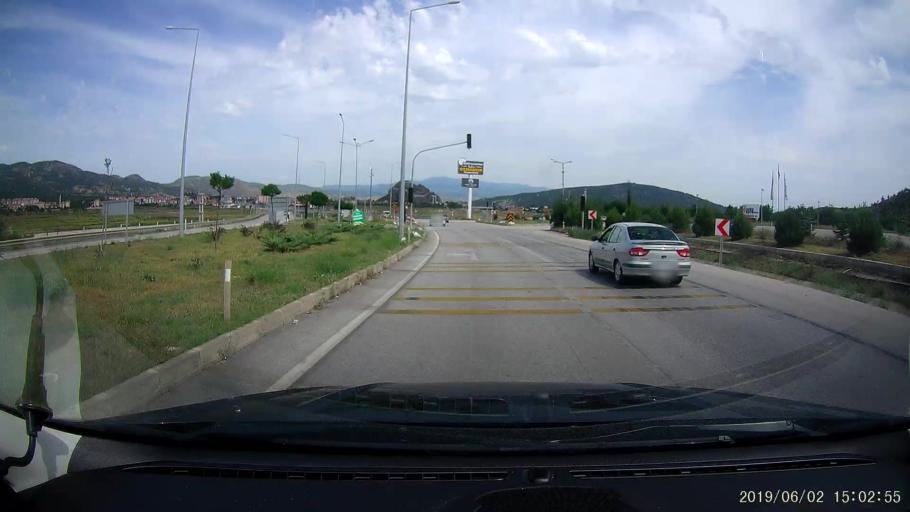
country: TR
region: Corum
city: Osmancik
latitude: 40.9777
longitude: 34.7734
